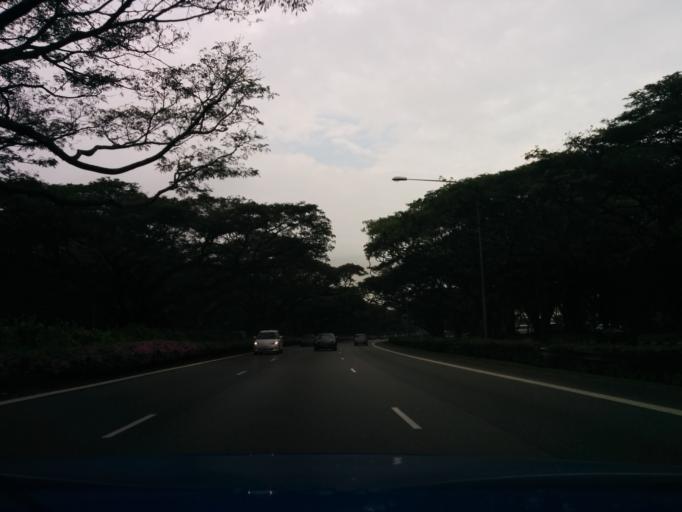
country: SG
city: Singapore
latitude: 1.3114
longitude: 103.9433
